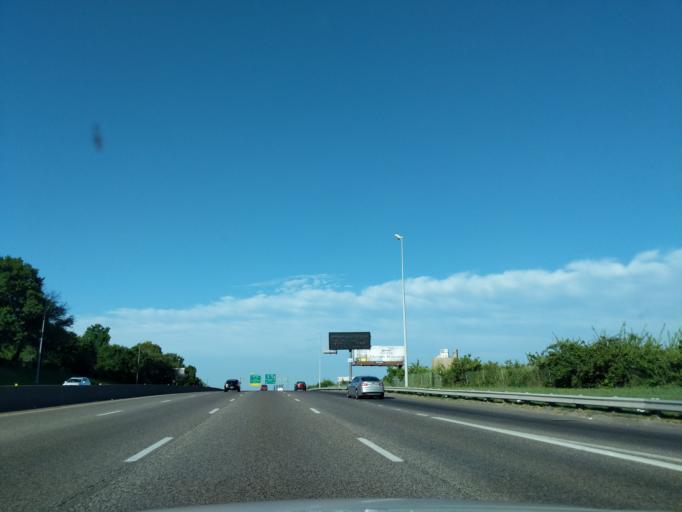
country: US
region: Illinois
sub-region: Saint Clair County
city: Cahokia
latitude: 38.5826
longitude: -90.2221
